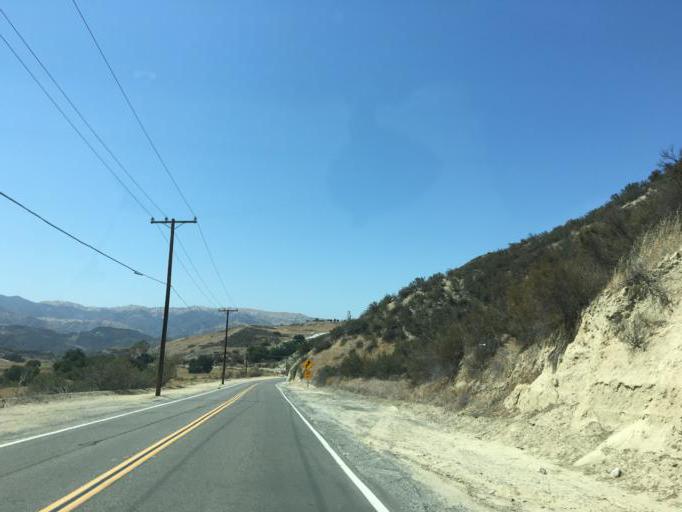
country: US
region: California
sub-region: Los Angeles County
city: Val Verde
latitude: 34.4373
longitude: -118.6586
